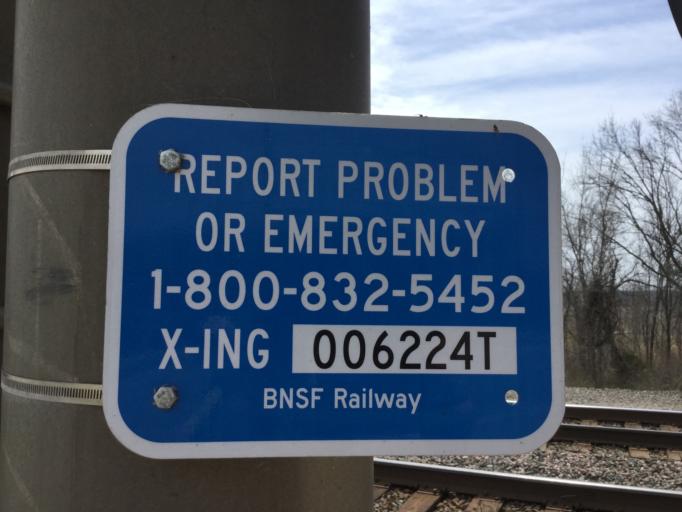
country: US
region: Kansas
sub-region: Franklin County
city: Ottawa
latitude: 38.6084
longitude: -95.3871
